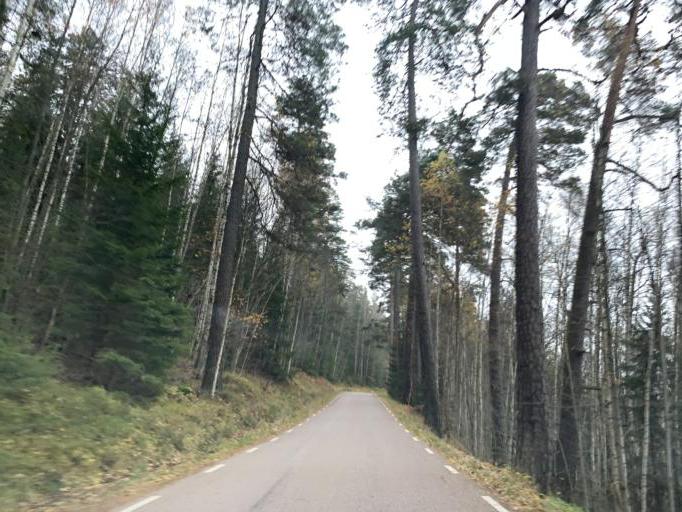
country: SE
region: Vaestmanland
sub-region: Surahammars Kommun
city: Surahammar
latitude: 59.6869
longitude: 16.0849
